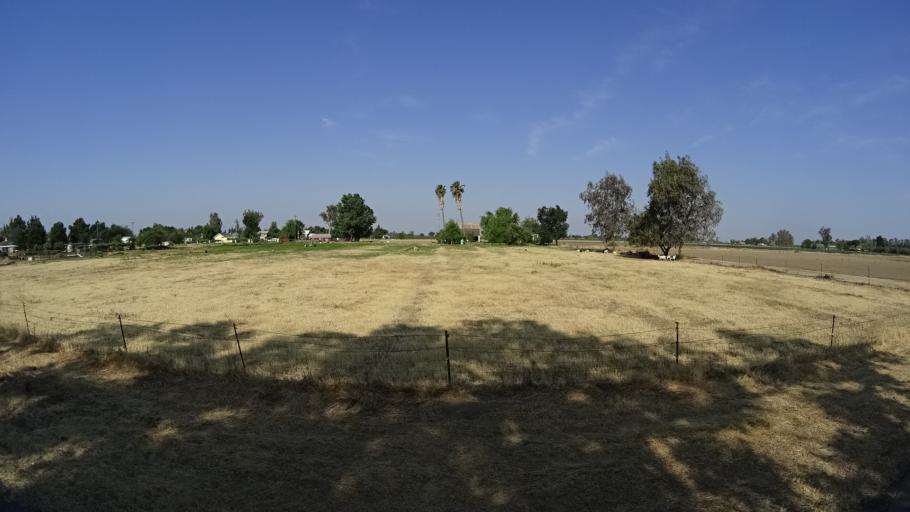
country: US
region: California
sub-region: Kings County
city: Lemoore
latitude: 36.3546
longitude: -119.8340
